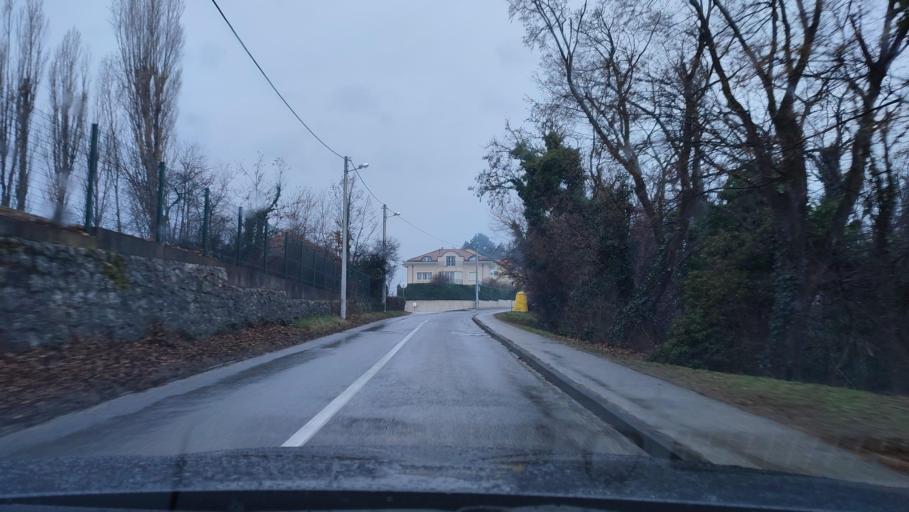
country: HR
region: Grad Zagreb
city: Zagreb
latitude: 45.8463
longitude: 15.9564
